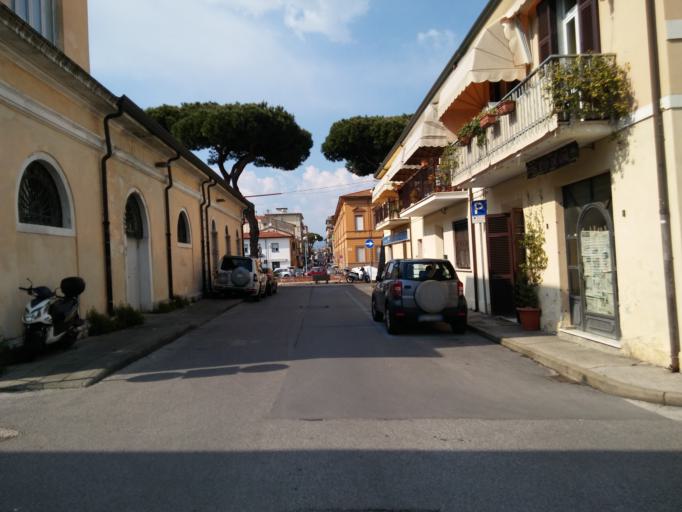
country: IT
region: Tuscany
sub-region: Provincia di Lucca
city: Viareggio
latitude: 43.8648
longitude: 10.2490
